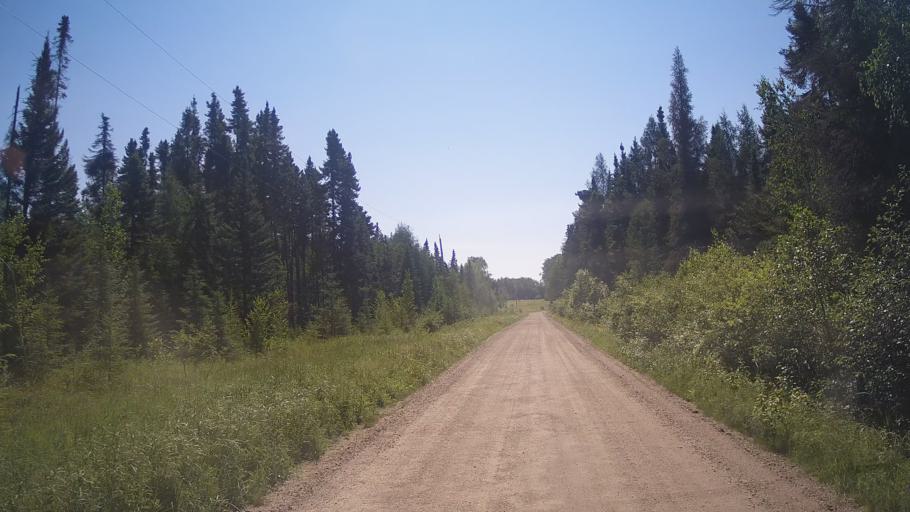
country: CA
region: Ontario
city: Dryden
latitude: 49.8190
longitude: -93.3352
